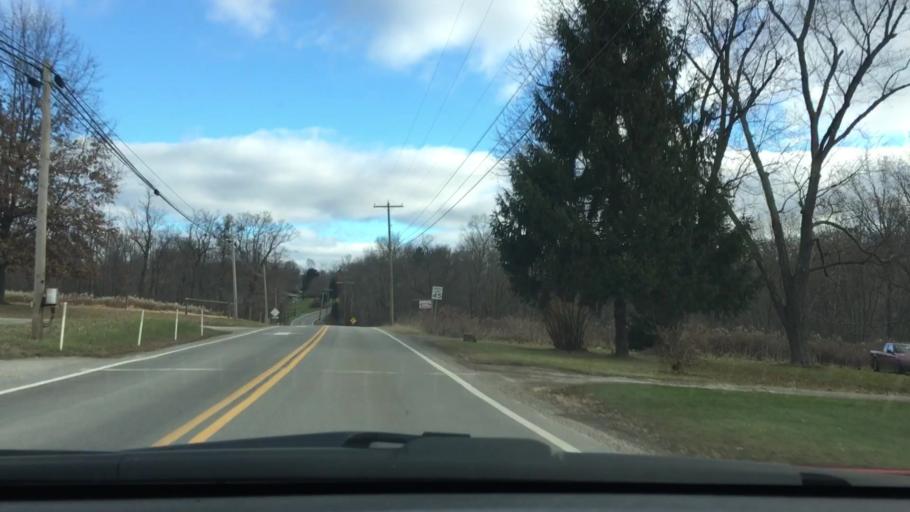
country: US
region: Pennsylvania
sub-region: Armstrong County
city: Orchard Hills
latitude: 40.6028
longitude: -79.5030
